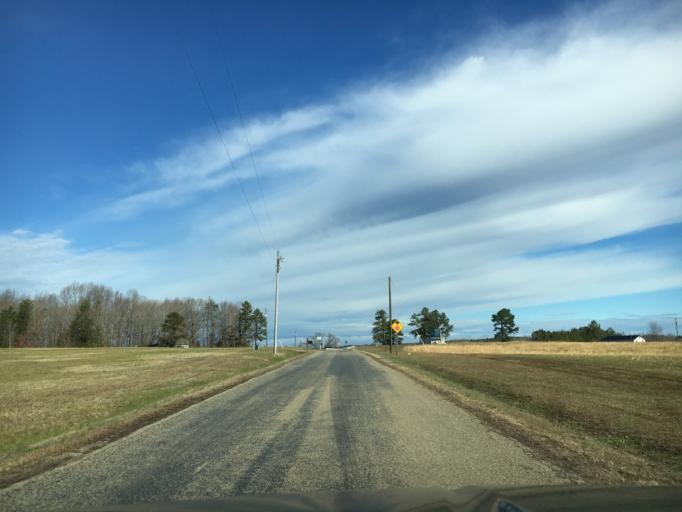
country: US
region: Virginia
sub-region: Nottoway County
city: Crewe
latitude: 37.2766
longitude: -78.2155
